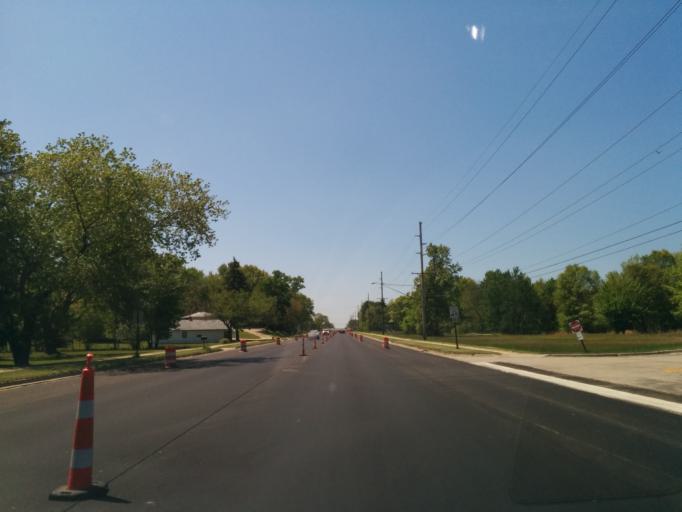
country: US
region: Michigan
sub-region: Berrien County
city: Bridgman
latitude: 41.9374
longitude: -86.5670
